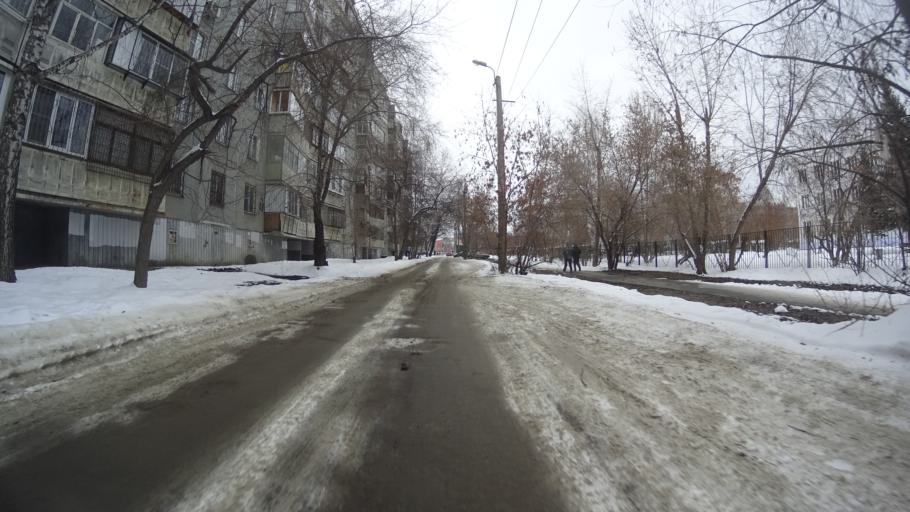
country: RU
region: Chelyabinsk
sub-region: Gorod Chelyabinsk
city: Chelyabinsk
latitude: 55.1762
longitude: 61.3412
